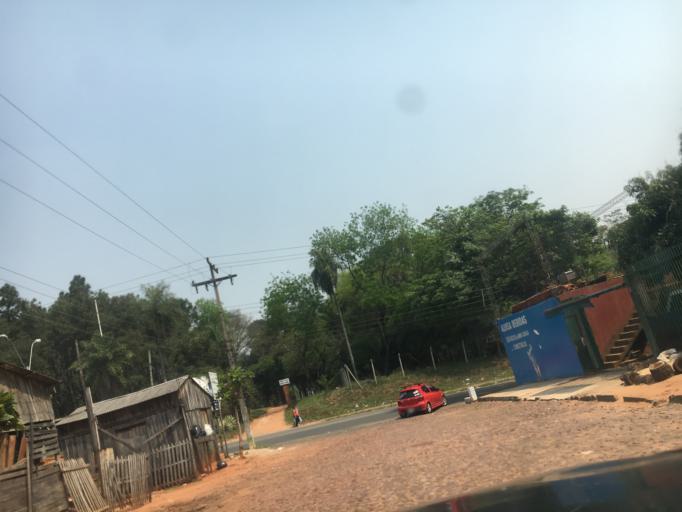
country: PY
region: Central
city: Villa Elisa
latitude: -25.3643
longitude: -57.5899
